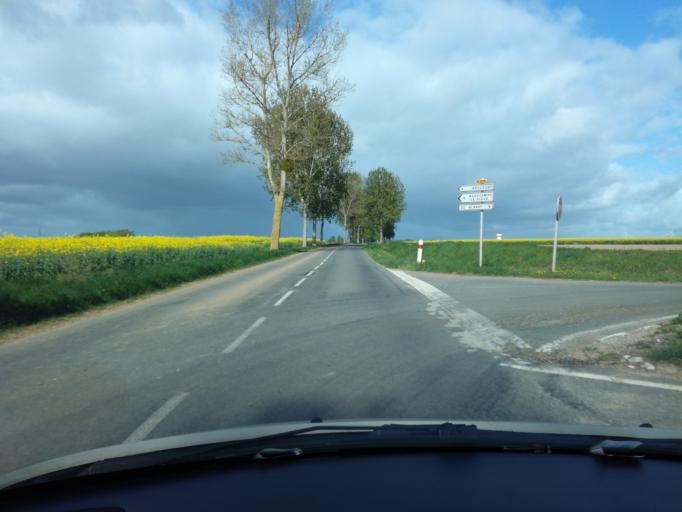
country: FR
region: Picardie
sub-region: Departement de la Somme
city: Hornoy-le-Bourg
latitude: 49.8542
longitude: 1.8602
